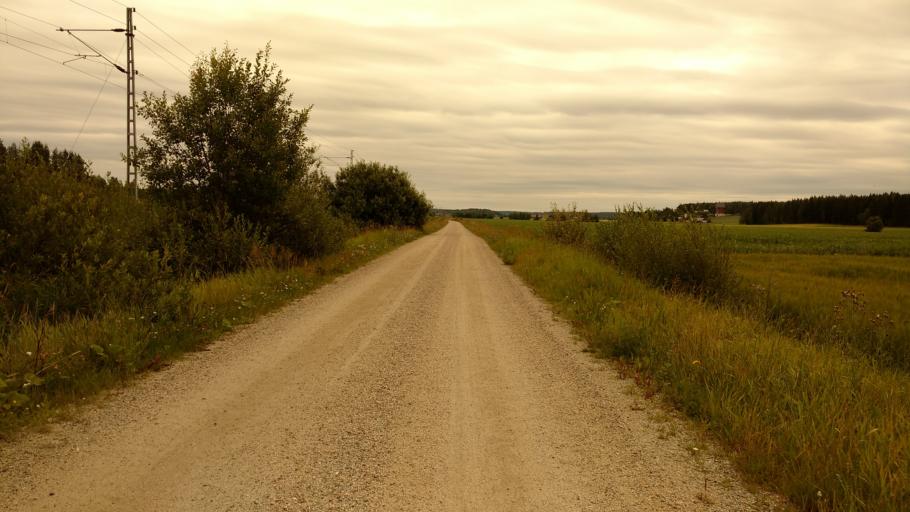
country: FI
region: Varsinais-Suomi
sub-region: Turku
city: Paimio
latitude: 60.4231
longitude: 22.8152
